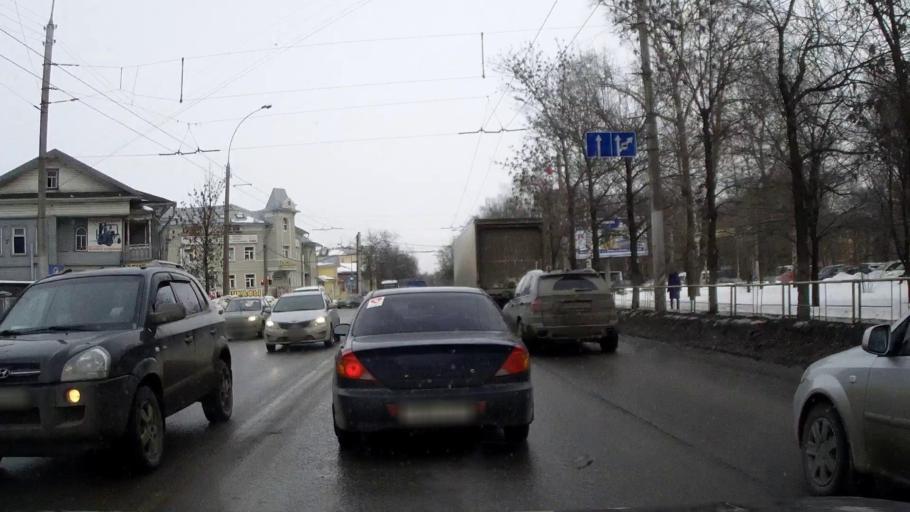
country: RU
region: Vologda
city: Vologda
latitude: 59.2204
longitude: 39.8696
